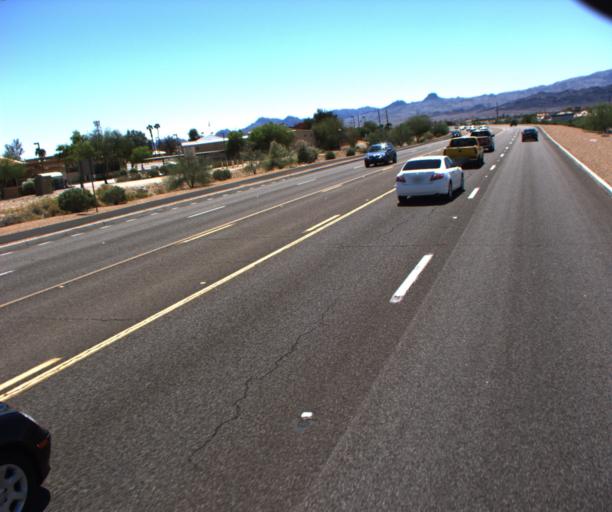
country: US
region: Arizona
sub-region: Mohave County
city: Lake Havasu City
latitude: 34.4815
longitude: -114.3494
